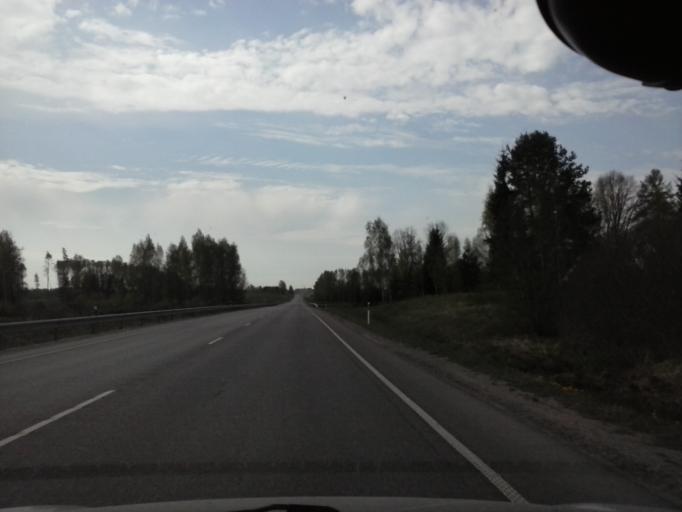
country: EE
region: Tartu
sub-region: UElenurme vald
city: Ulenurme
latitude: 58.1708
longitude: 26.6914
